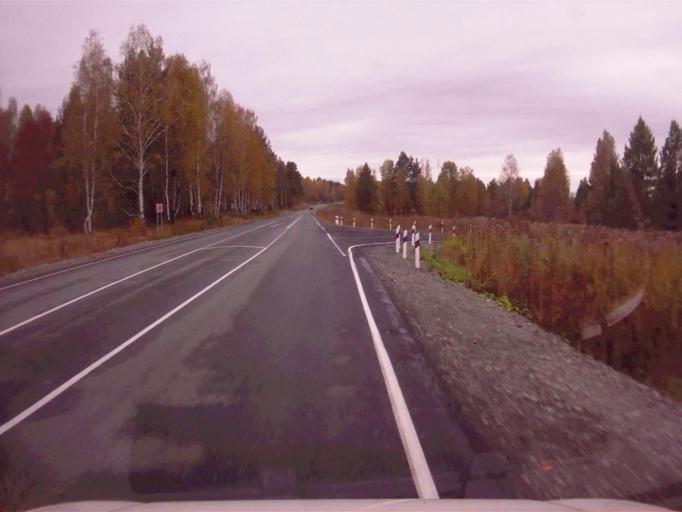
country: RU
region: Chelyabinsk
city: Nyazepetrovsk
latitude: 56.0443
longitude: 59.7674
